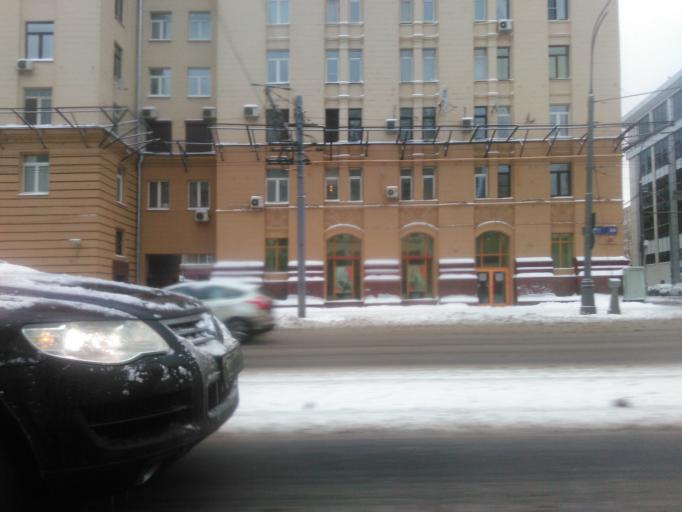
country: RU
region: Moscow
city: Mar'ina Roshcha
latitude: 55.7867
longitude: 37.6354
